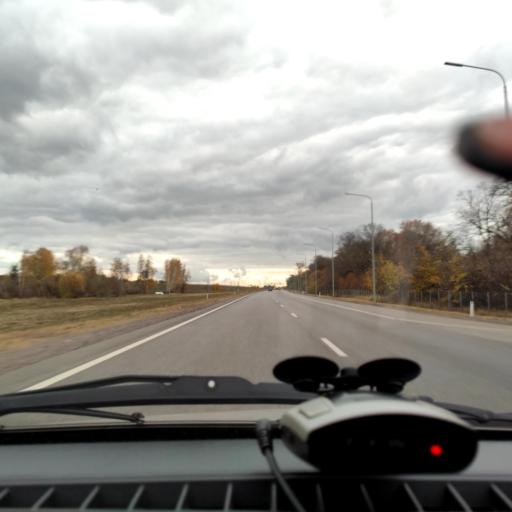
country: RU
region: Voronezj
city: Podgornoye
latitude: 51.8417
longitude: 39.2143
